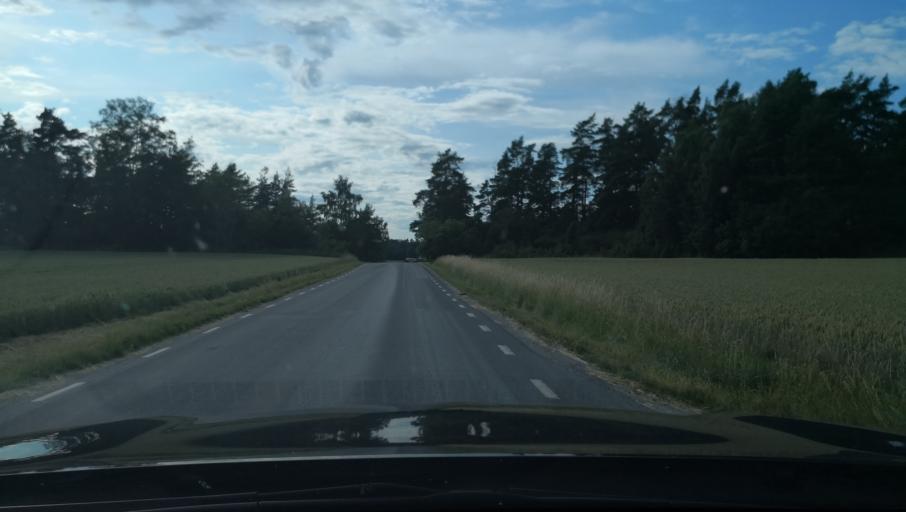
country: SE
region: Uppsala
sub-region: Enkopings Kommun
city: Orsundsbro
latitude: 59.6837
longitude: 17.3999
